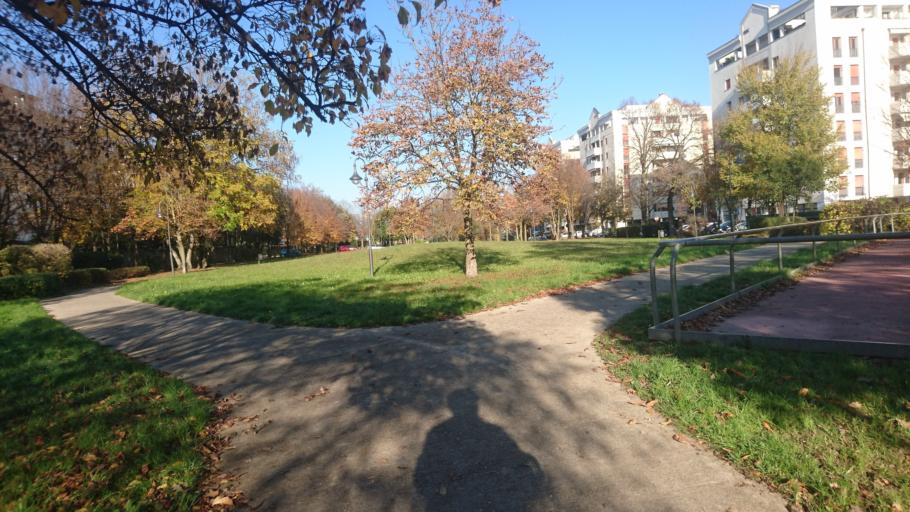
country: IT
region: Veneto
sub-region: Provincia di Padova
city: Caselle
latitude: 45.4081
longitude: 11.8459
